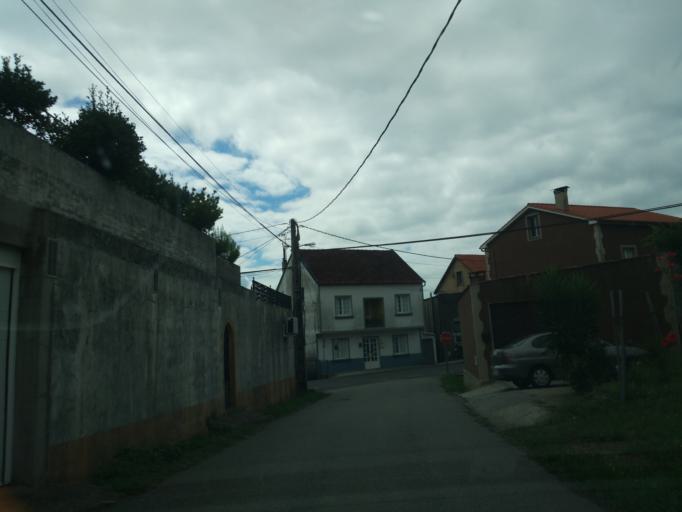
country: ES
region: Galicia
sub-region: Provincia da Coruna
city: Boiro
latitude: 42.6483
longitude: -8.8606
